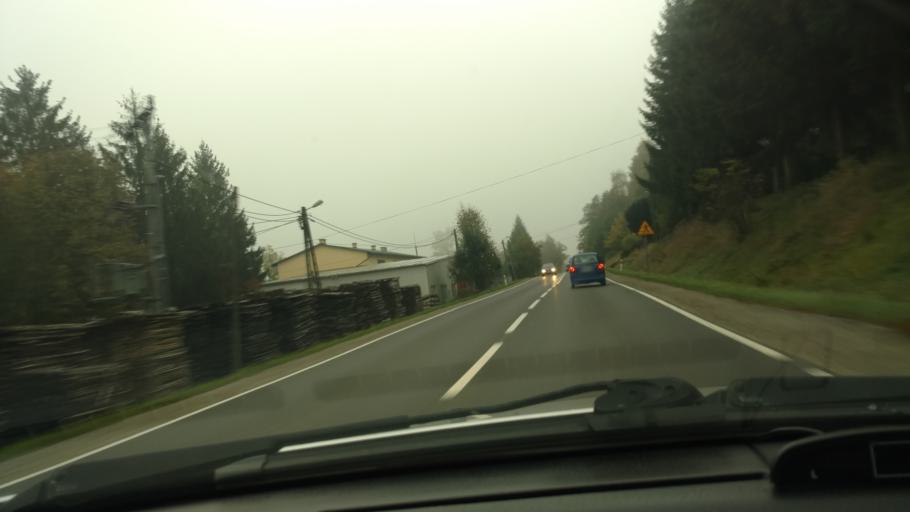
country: PL
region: Subcarpathian Voivodeship
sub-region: Powiat strzyzowski
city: Frysztak
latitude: 49.8361
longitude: 21.6119
